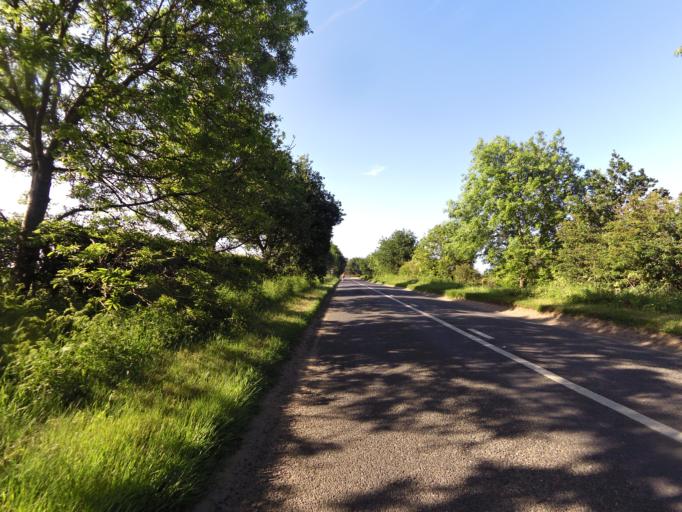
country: GB
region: England
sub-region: Suffolk
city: Woodbridge
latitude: 52.0766
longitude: 1.3635
